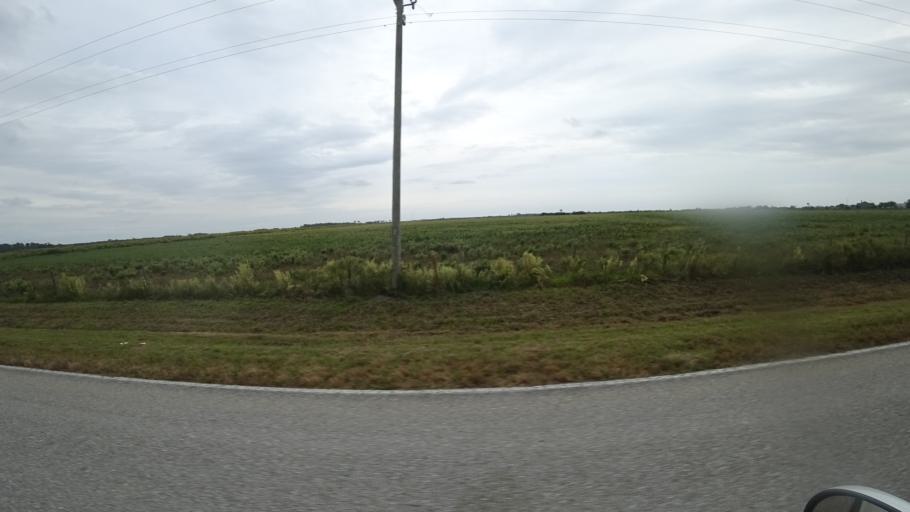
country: US
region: Florida
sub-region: Sarasota County
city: Lake Sarasota
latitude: 27.3078
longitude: -82.1831
